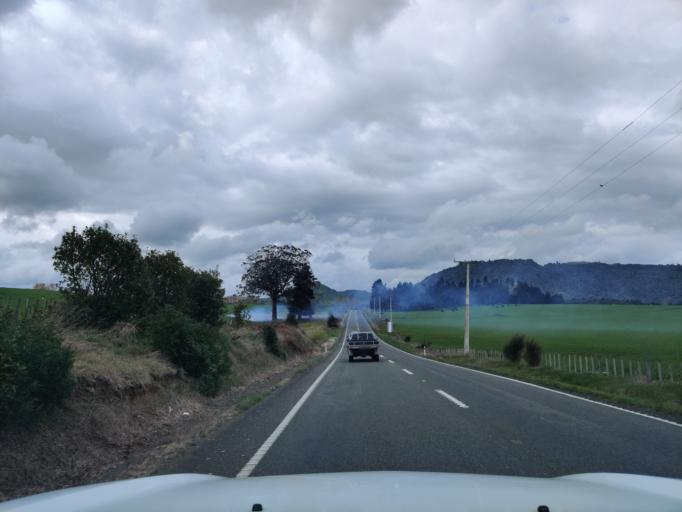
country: NZ
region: Manawatu-Wanganui
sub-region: Ruapehu District
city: Waiouru
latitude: -39.4876
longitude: 175.2978
